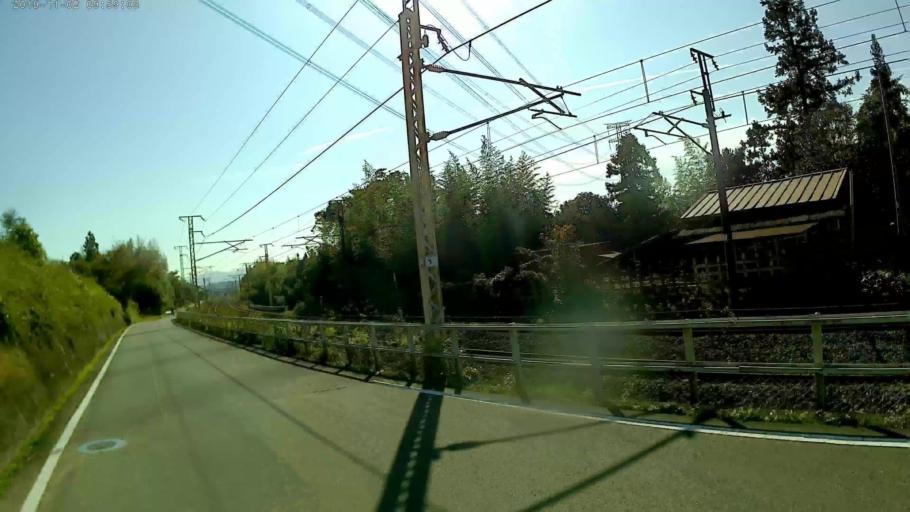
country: JP
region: Gunma
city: Annaka
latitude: 36.3201
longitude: 138.7802
